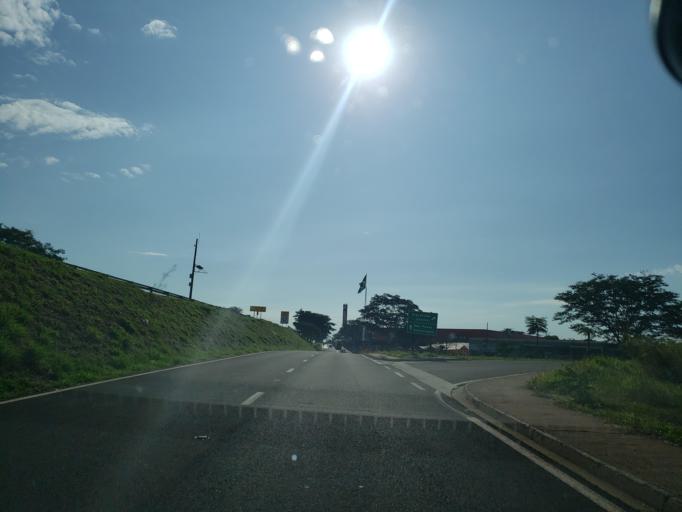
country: BR
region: Sao Paulo
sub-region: Aracatuba
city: Aracatuba
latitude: -21.2133
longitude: -50.4659
